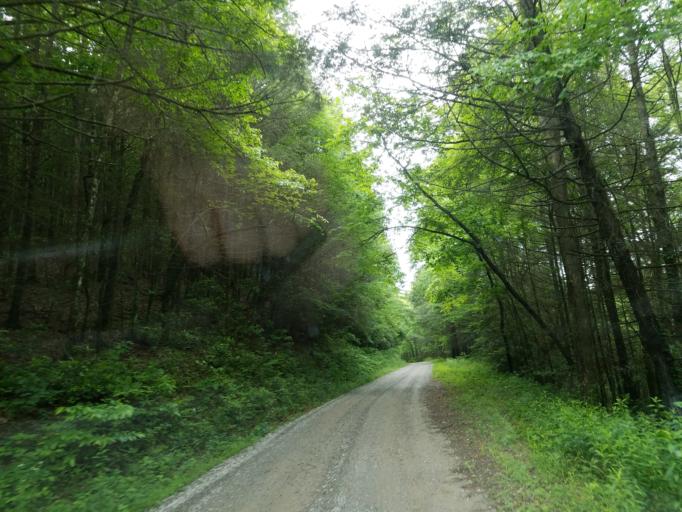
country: US
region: Georgia
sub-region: Union County
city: Blairsville
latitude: 34.7550
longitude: -83.9982
